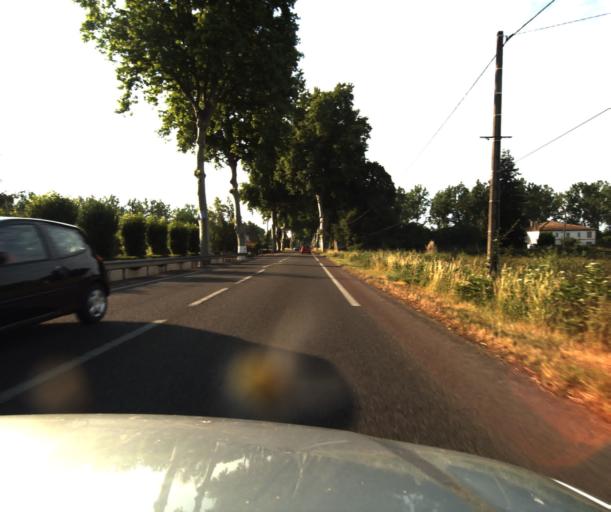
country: FR
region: Midi-Pyrenees
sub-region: Departement du Tarn-et-Garonne
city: Moissac
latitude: 44.0712
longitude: 1.0945
